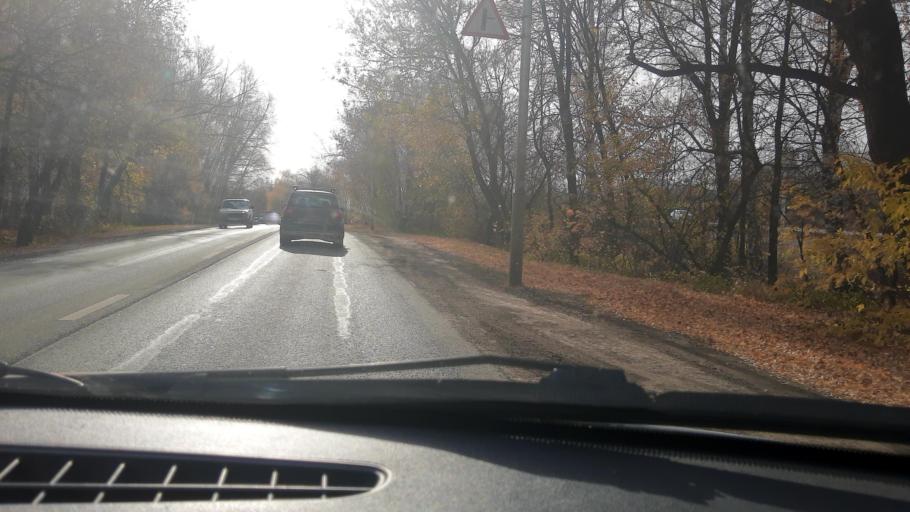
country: RU
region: Bashkortostan
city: Avdon
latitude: 54.7185
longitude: 55.8087
